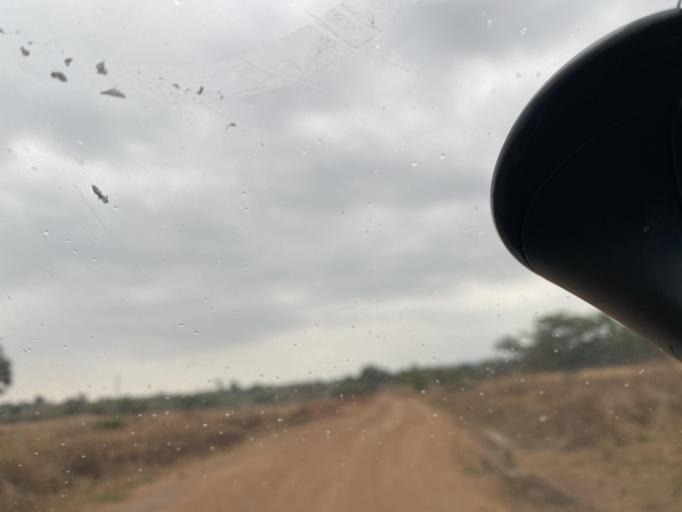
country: ZM
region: Lusaka
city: Chongwe
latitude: -15.1657
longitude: 28.7631
